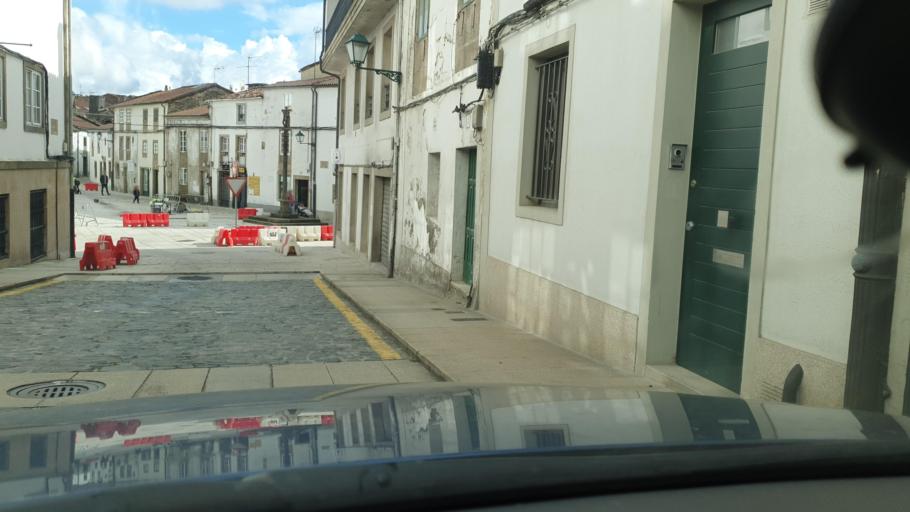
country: ES
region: Galicia
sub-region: Provincia da Coruna
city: Santiago de Compostela
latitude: 42.8821
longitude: -8.5353
